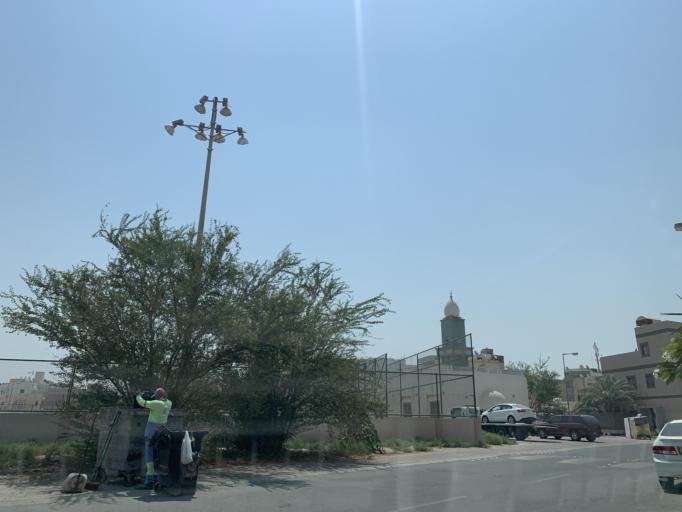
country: BH
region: Manama
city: Jidd Hafs
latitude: 26.2061
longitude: 50.5191
